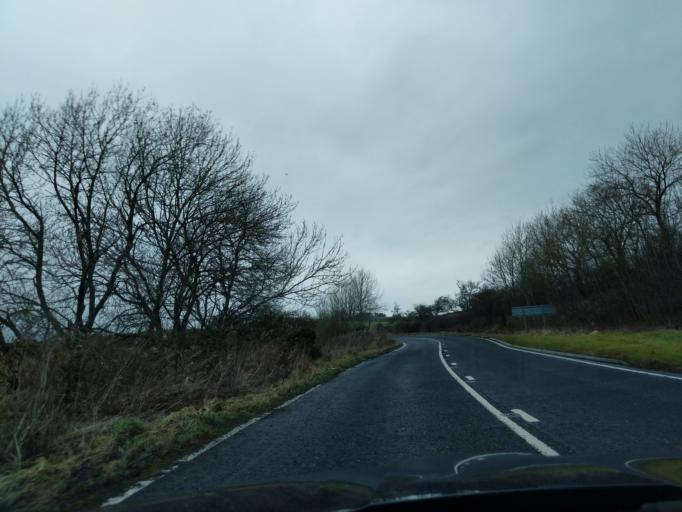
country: GB
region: England
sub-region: Northumberland
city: Rothley
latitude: 55.1568
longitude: -2.0116
